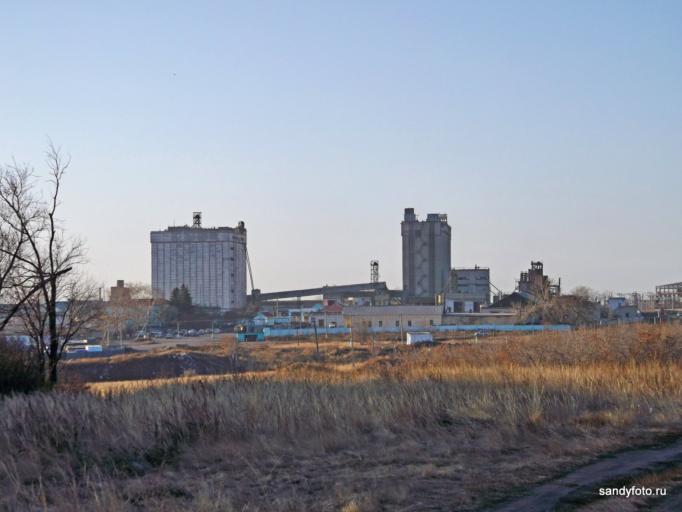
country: RU
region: Chelyabinsk
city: Troitsk
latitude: 54.1021
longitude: 61.5947
